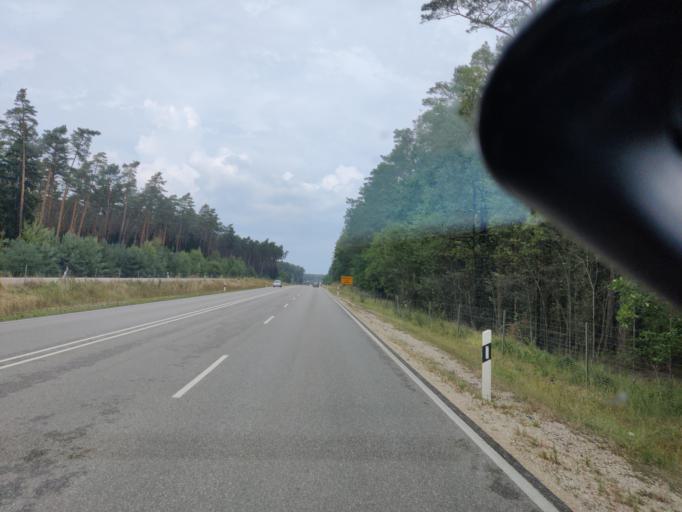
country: DE
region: Bavaria
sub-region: Regierungsbezirk Mittelfranken
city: Rottenbach
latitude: 49.1332
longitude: 11.0268
